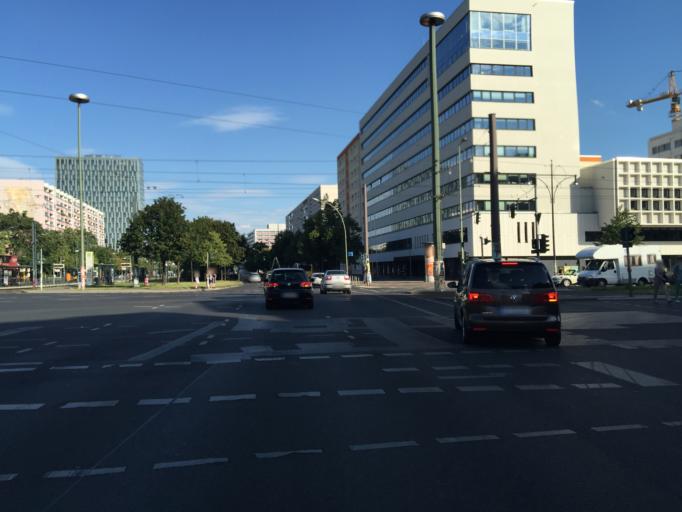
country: DE
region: Berlin
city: Berlin
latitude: 52.5270
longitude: 13.4152
